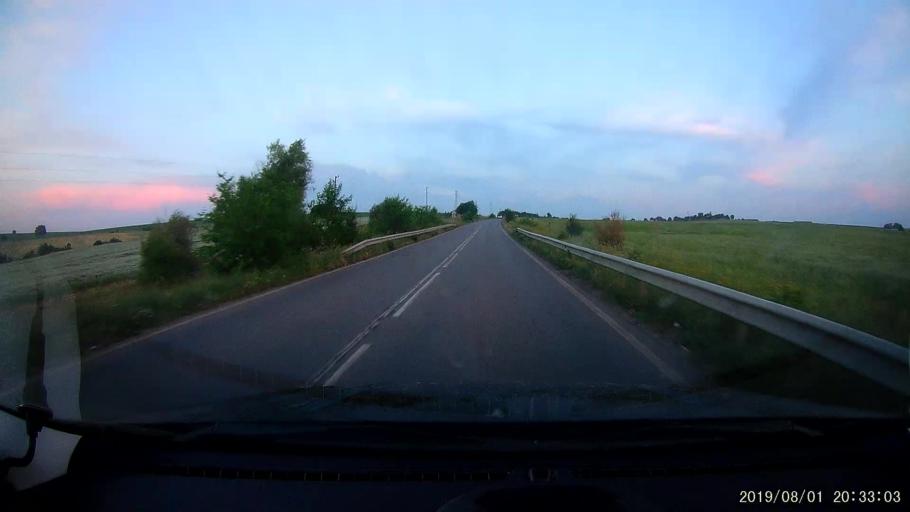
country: BG
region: Yambol
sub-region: Obshtina Elkhovo
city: Elkhovo
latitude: 42.1122
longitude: 26.5314
